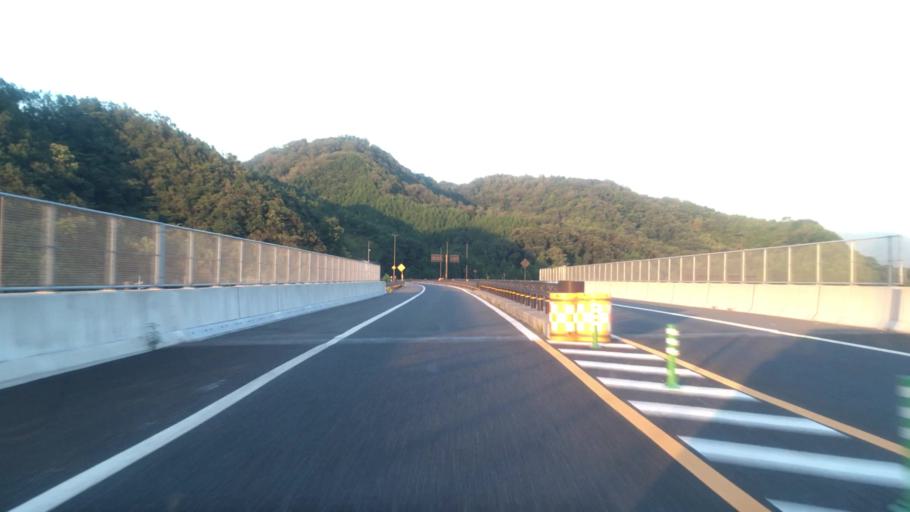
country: JP
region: Tottori
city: Tottori
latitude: 35.5731
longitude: 134.3153
